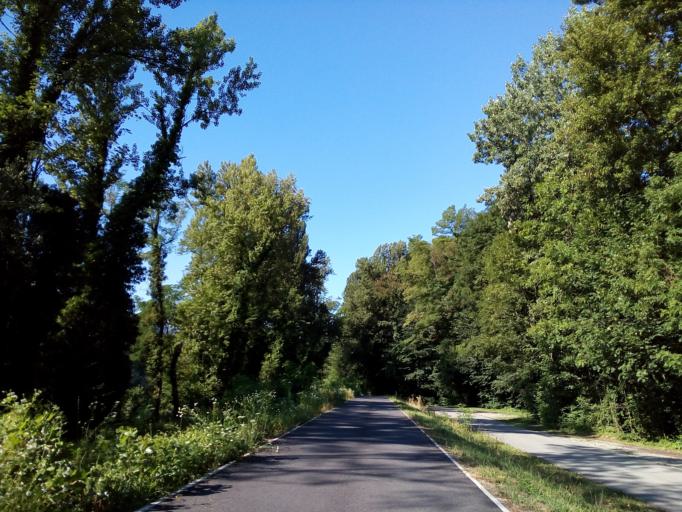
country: FR
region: Rhone-Alpes
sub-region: Departement de l'Isere
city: Le Versoud
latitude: 45.2234
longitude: 5.8446
